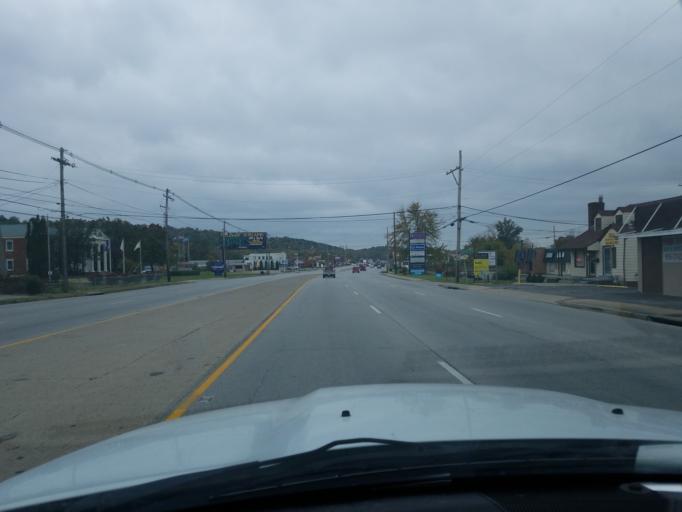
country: US
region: Kentucky
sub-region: Jefferson County
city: Pleasure Ridge Park
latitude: 38.1470
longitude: -85.8381
